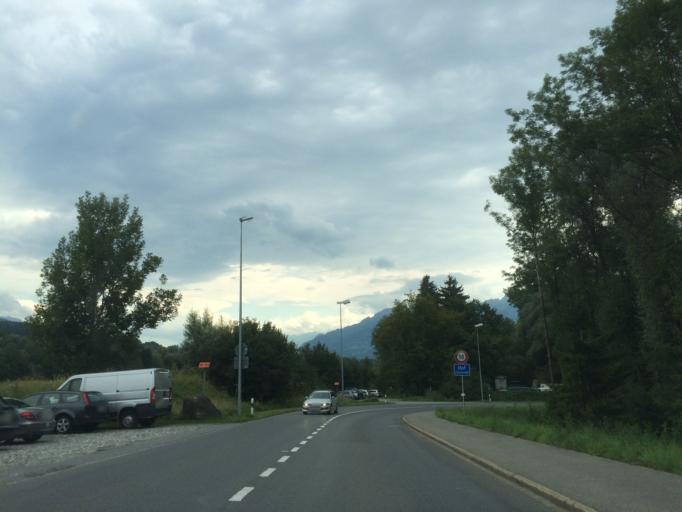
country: LI
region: Ruggell
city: Ruggell
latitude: 47.2433
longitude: 9.5186
